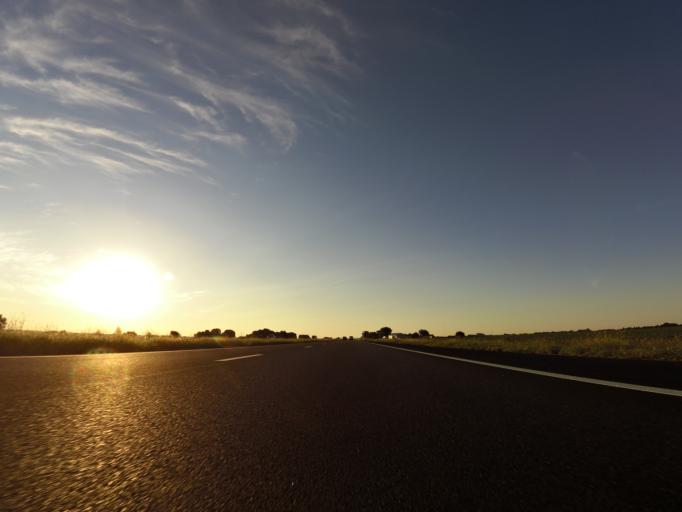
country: US
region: Kansas
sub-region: Sedgwick County
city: Colwich
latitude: 37.8494
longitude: -97.5975
